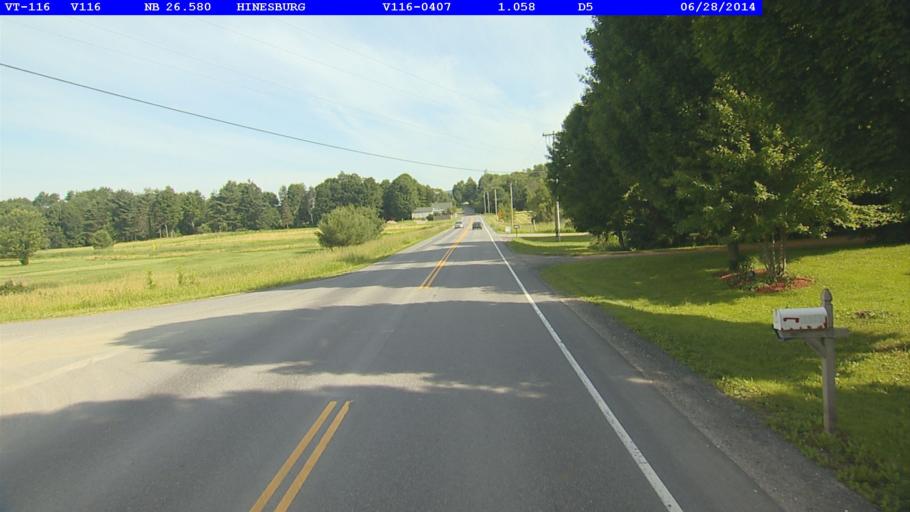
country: US
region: Vermont
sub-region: Chittenden County
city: Hinesburg
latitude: 44.2951
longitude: -73.0718
